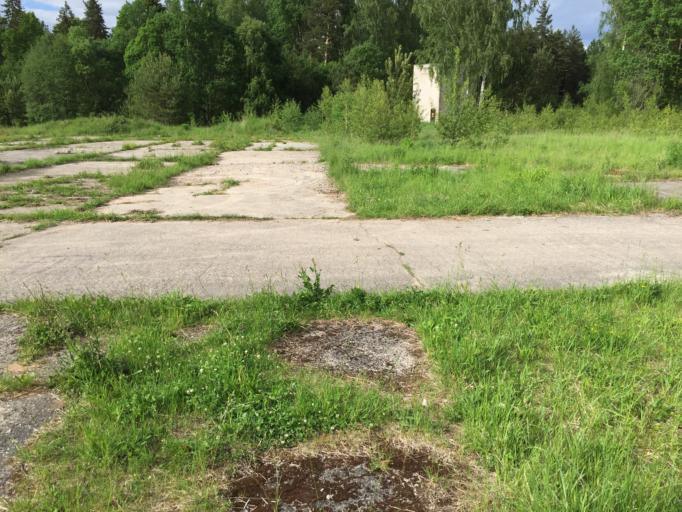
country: LV
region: Dobeles Rajons
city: Dobele
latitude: 56.6384
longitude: 23.1742
